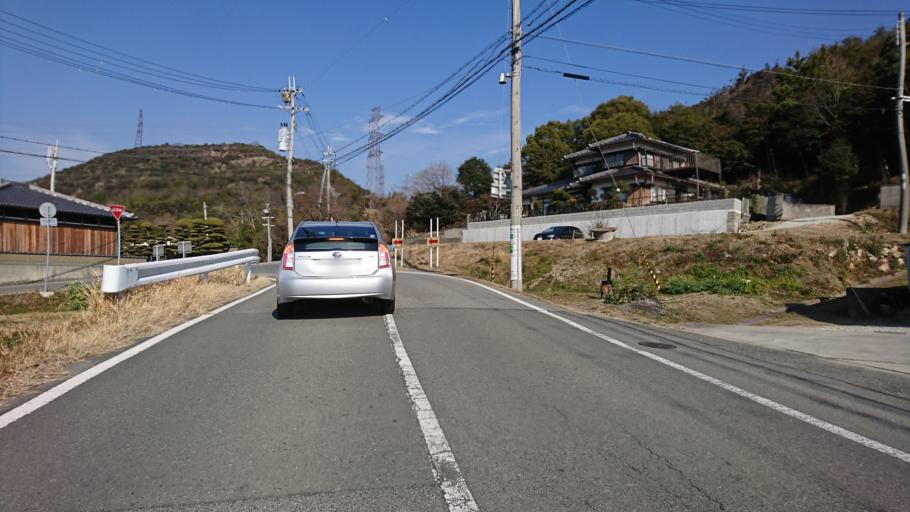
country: JP
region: Hyogo
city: Kakogawacho-honmachi
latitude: 34.7959
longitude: 134.8396
